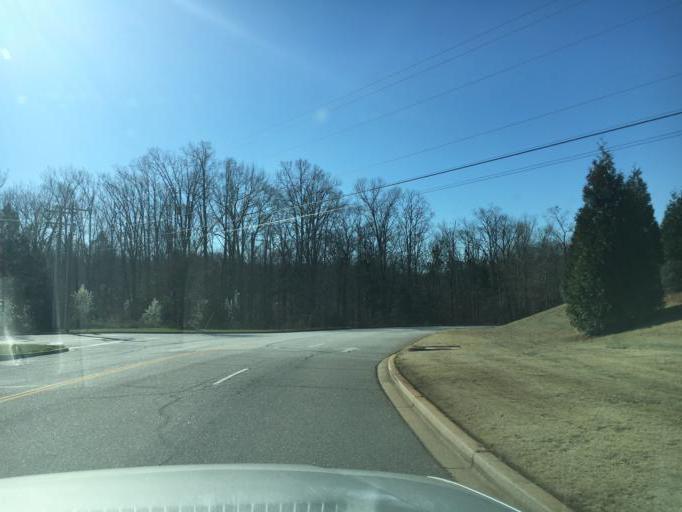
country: US
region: South Carolina
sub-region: Spartanburg County
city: Wellford
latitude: 34.8976
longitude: -82.0746
